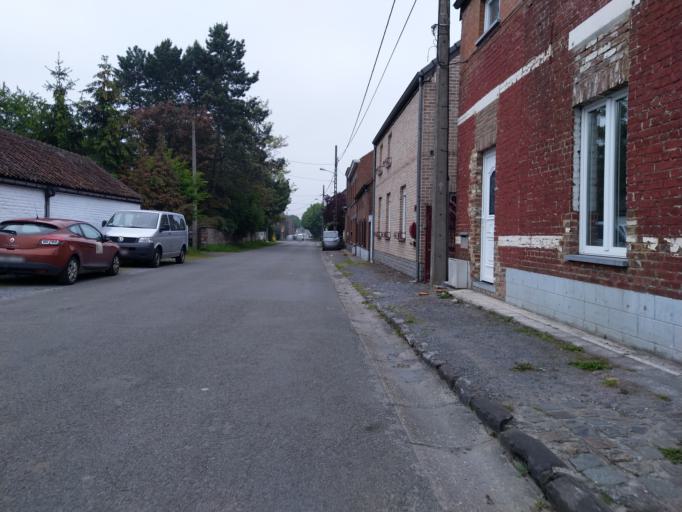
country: BE
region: Wallonia
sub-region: Province du Hainaut
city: Jurbise
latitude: 50.4845
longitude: 3.9155
